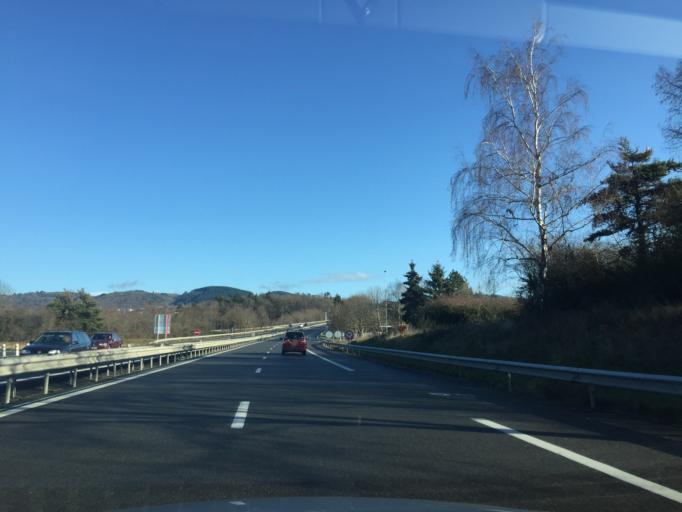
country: FR
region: Auvergne
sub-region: Departement du Puy-de-Dome
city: Peschadoires
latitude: 45.8613
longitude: 3.5003
